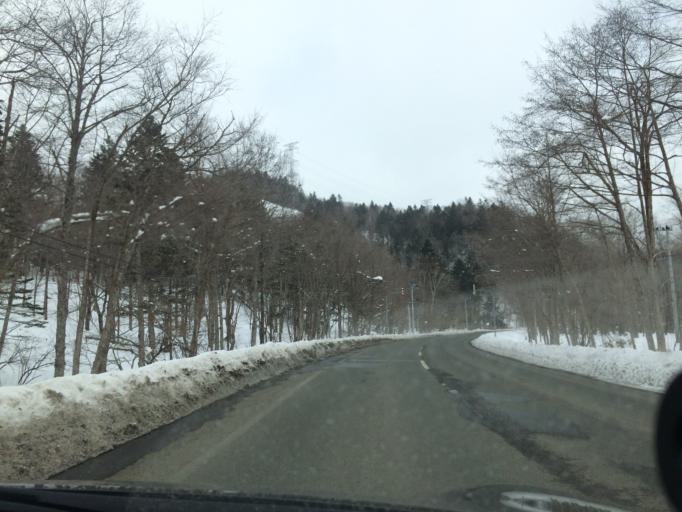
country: JP
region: Hokkaido
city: Shimo-furano
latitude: 43.0518
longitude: 142.4820
